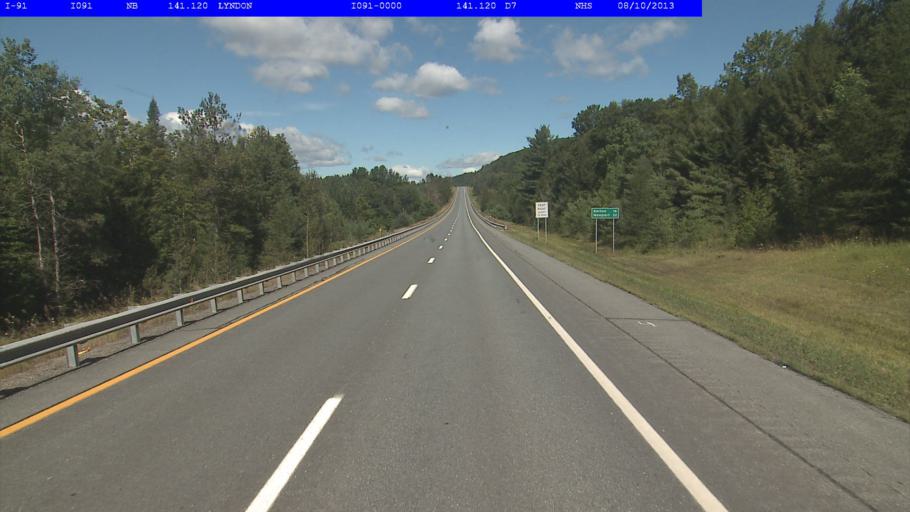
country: US
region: Vermont
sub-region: Caledonia County
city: Lyndonville
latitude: 44.5689
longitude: -72.0359
